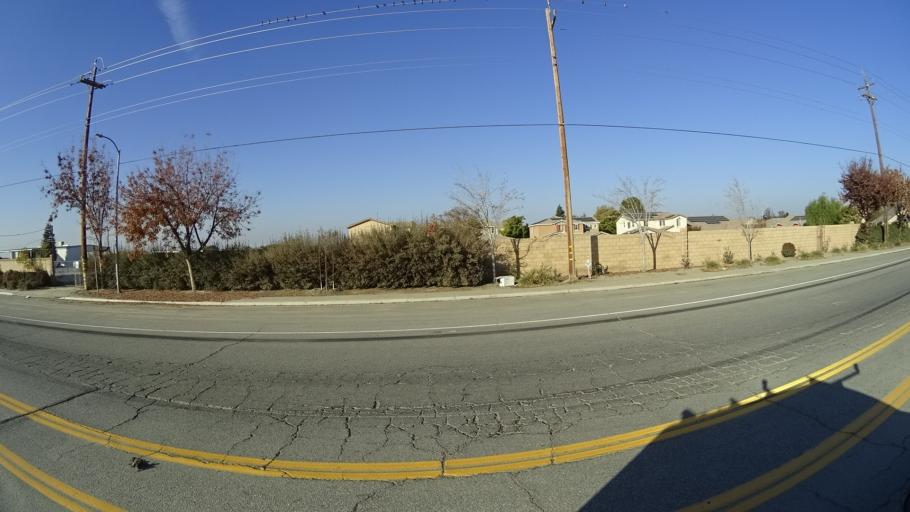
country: US
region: California
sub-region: Kern County
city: Rosedale
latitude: 35.2962
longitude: -119.1386
